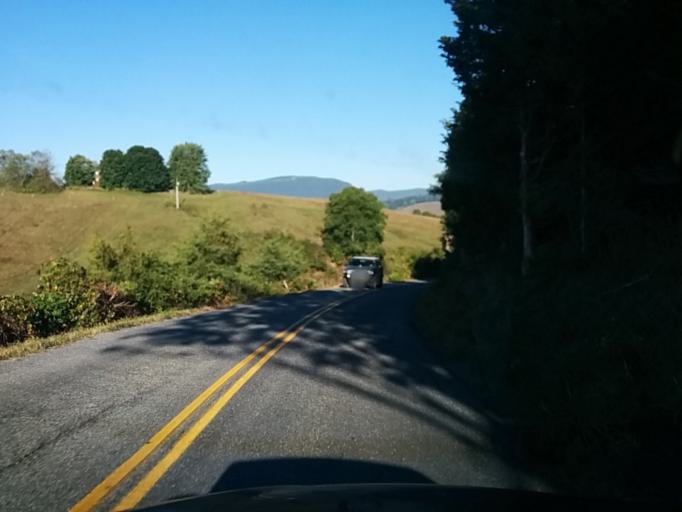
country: US
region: Virginia
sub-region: City of Lexington
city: Lexington
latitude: 37.7482
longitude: -79.5519
